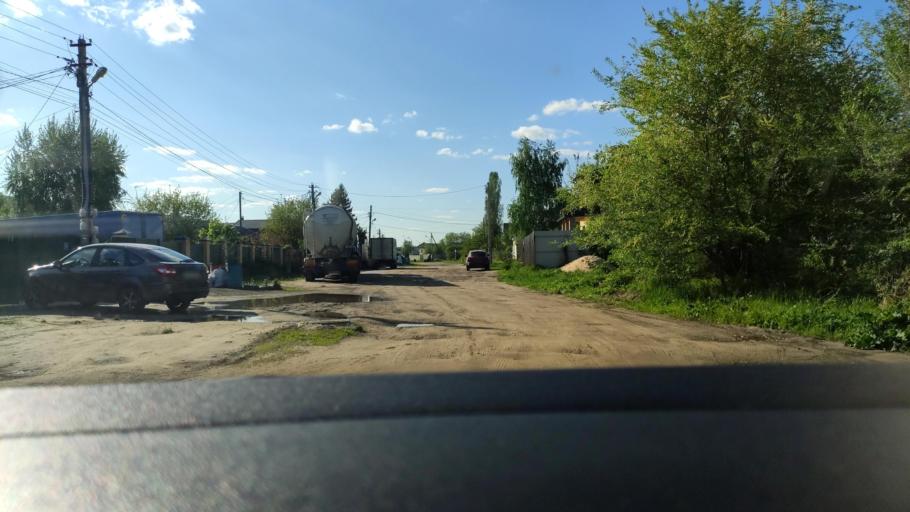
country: RU
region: Voronezj
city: Pridonskoy
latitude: 51.6465
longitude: 39.0965
